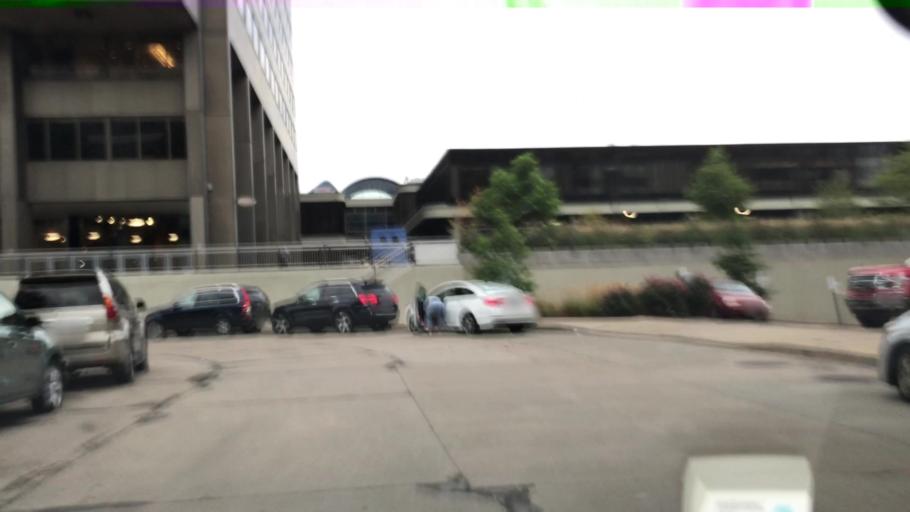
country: US
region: Pennsylvania
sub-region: Allegheny County
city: Pittsburgh
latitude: 40.4523
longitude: -80.0045
